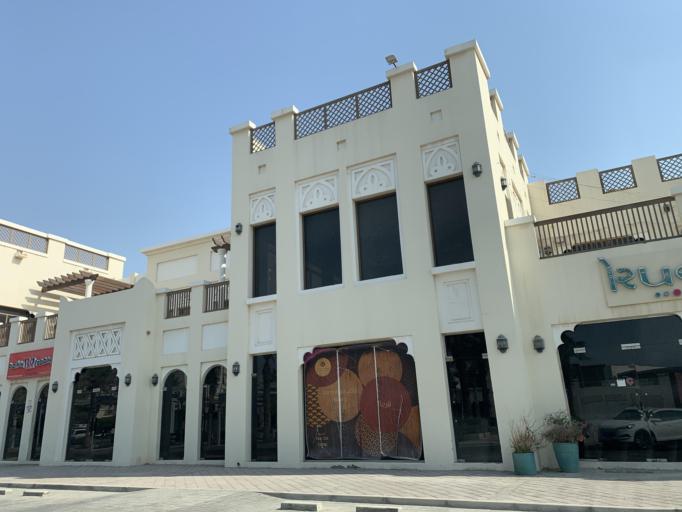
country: BH
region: Northern
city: Madinat `Isa
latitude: 26.1946
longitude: 50.5127
